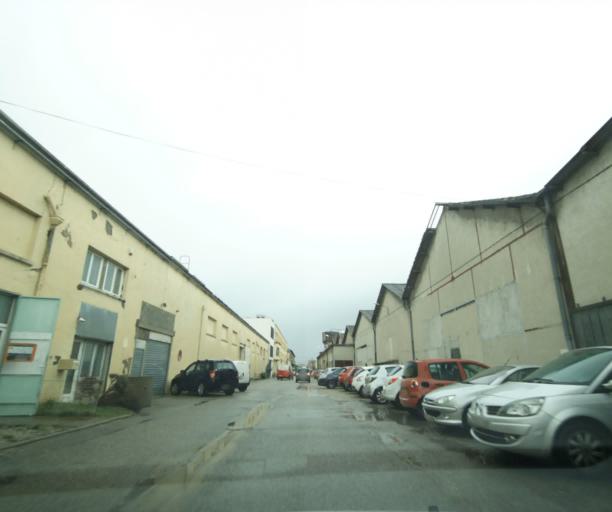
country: FR
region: Rhone-Alpes
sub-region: Departement de la Drome
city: Bourg-les-Valence
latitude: 44.9537
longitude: 4.8904
